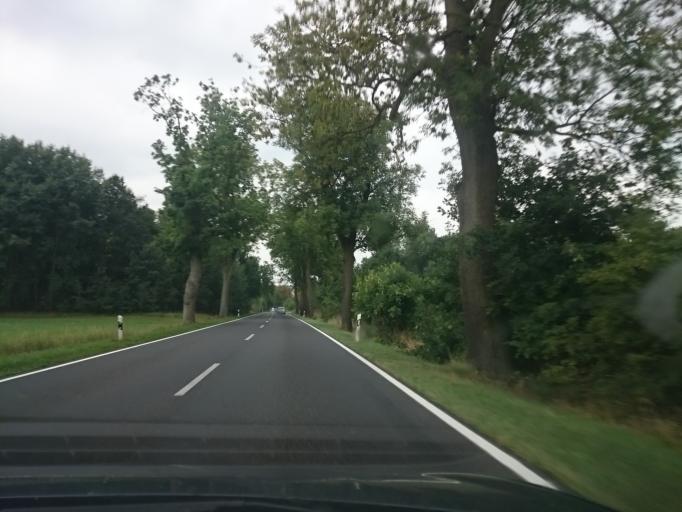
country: DE
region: Brandenburg
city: Gransee
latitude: 53.0258
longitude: 13.1852
